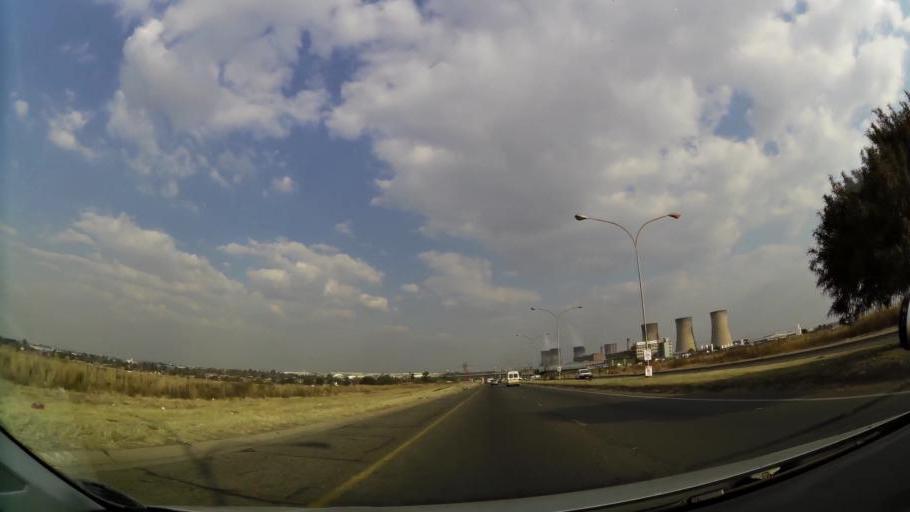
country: ZA
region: Gauteng
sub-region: City of Johannesburg Metropolitan Municipality
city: Modderfontein
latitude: -26.1046
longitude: 28.1965
